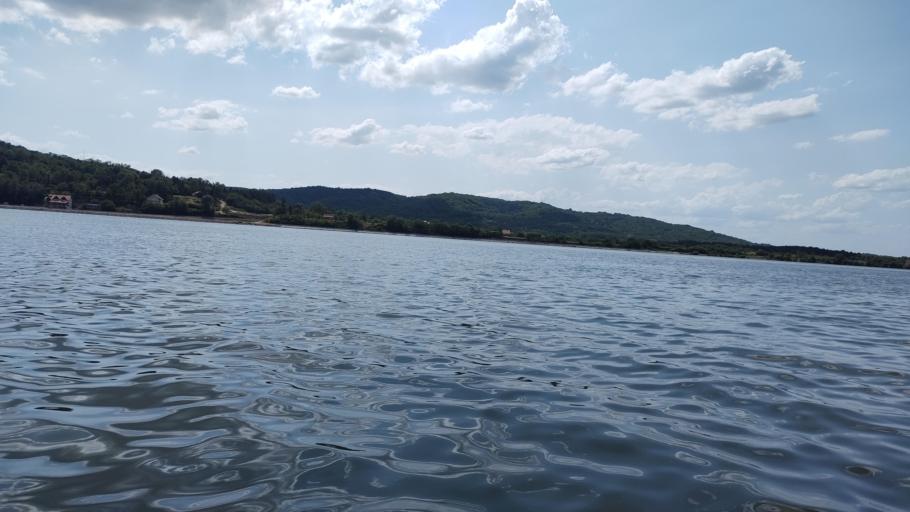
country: RS
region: Central Serbia
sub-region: Branicevski Okrug
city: Golubac
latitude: 44.6682
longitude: 21.6208
